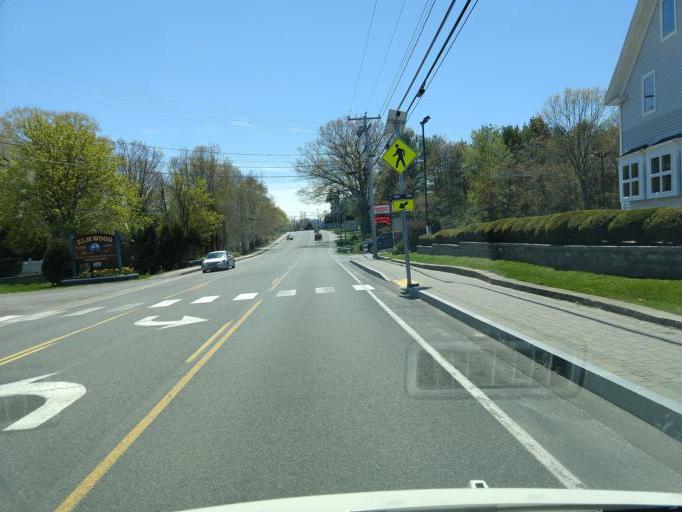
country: US
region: Maine
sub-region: York County
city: Wells Beach Station
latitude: 43.3160
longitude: -70.5837
